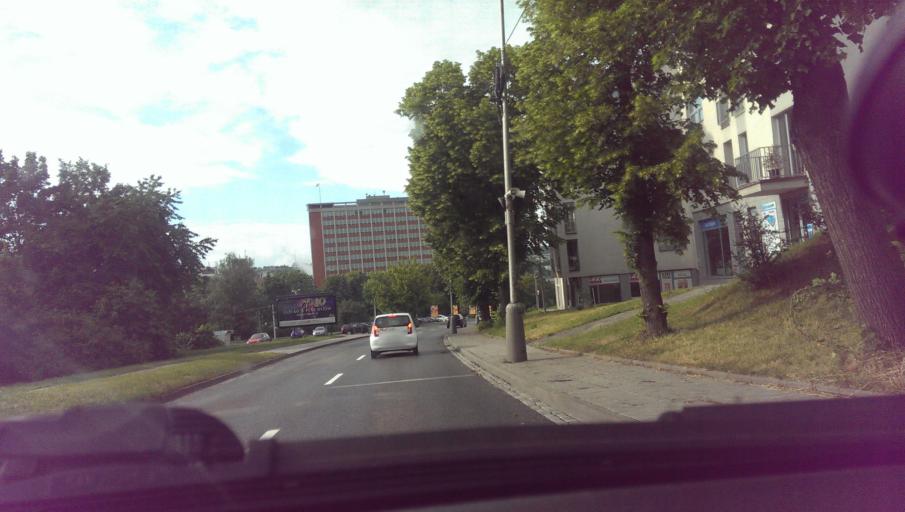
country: CZ
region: Zlin
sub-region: Okres Zlin
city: Zlin
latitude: 49.2200
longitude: 17.6597
